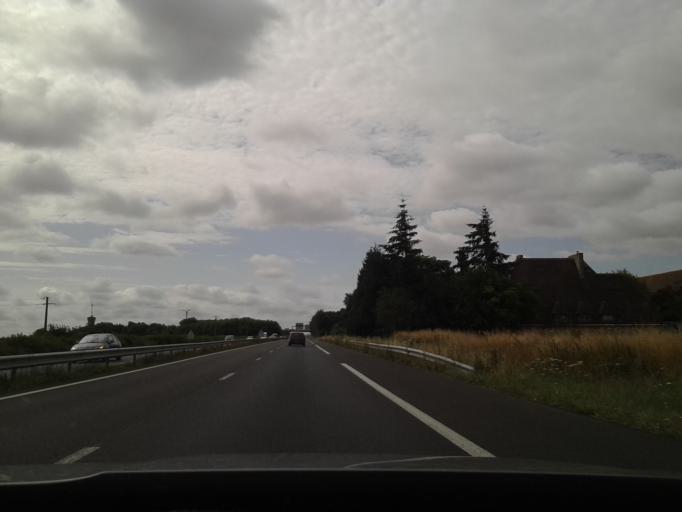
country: FR
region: Lower Normandy
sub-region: Departement du Calvados
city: Bretteville-sur-Laize
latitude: 49.0476
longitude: -0.2827
